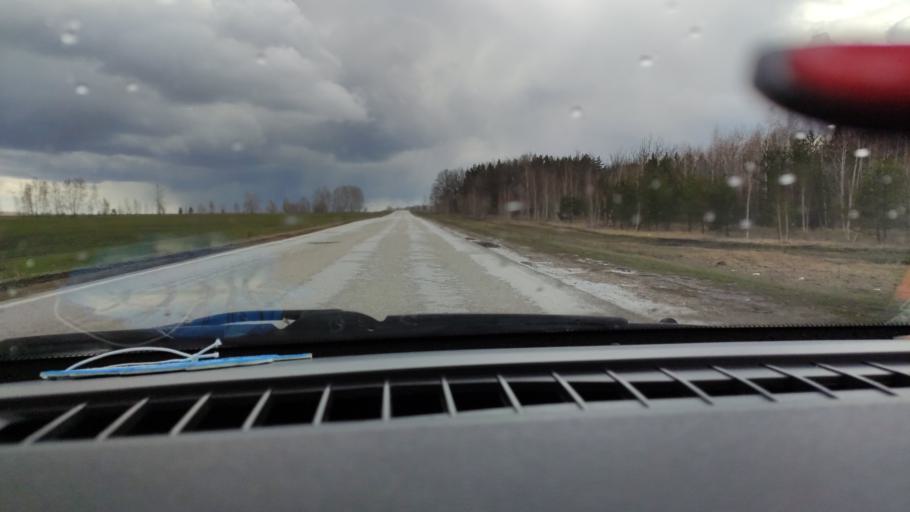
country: RU
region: Samara
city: Povolzhskiy
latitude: 53.8022
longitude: 49.7820
